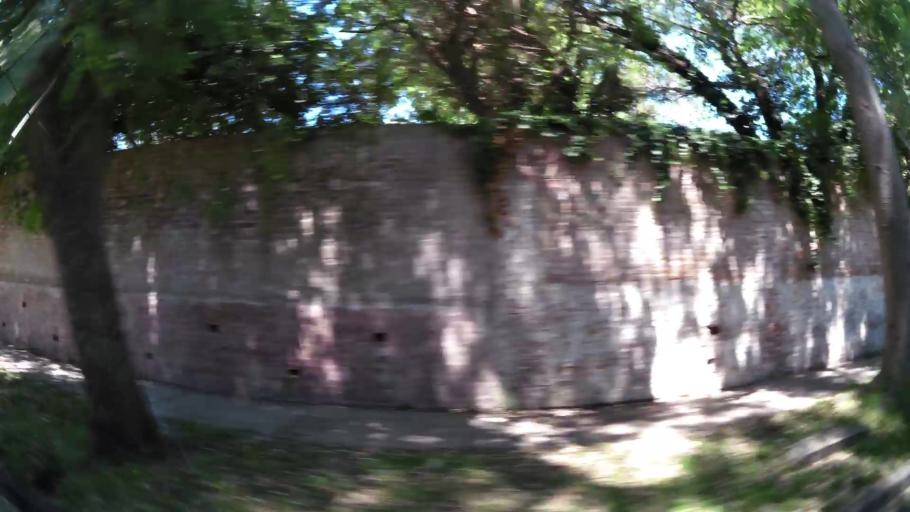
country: AR
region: Buenos Aires
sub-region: Partido de San Isidro
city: San Isidro
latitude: -34.4557
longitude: -58.5161
